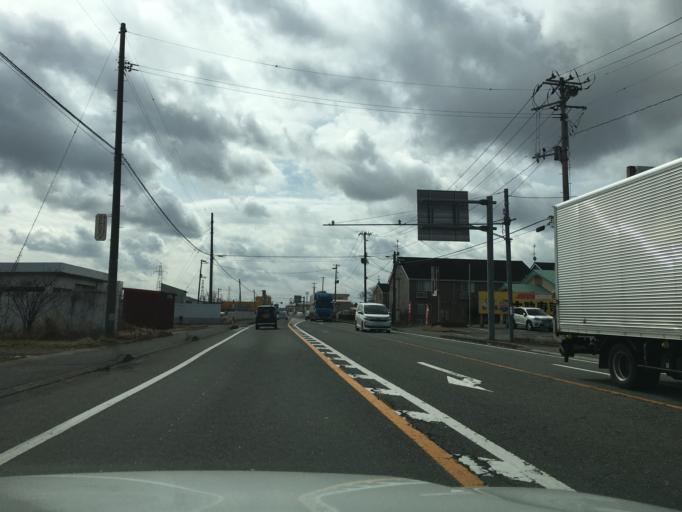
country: JP
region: Akita
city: Tenno
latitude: 39.9491
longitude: 140.0833
